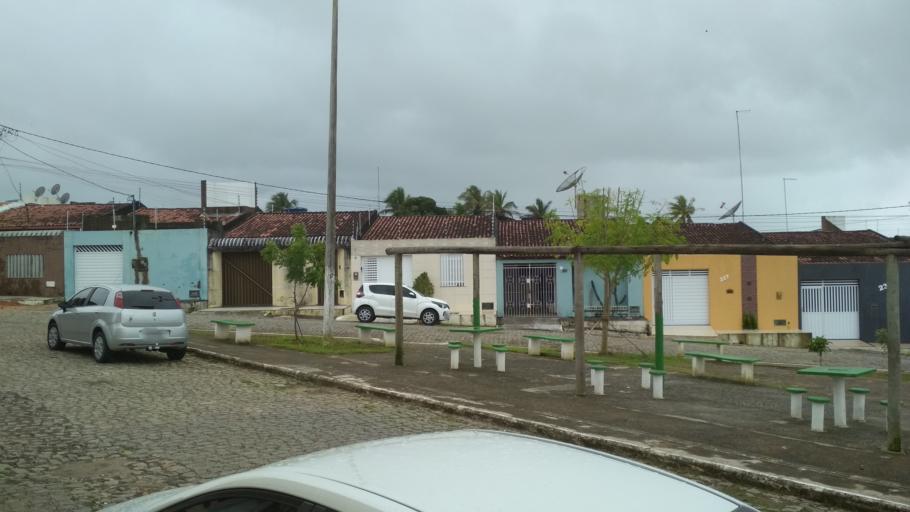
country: BR
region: Sergipe
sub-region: Lagarto
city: Lagarto
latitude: -10.9076
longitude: -37.6738
